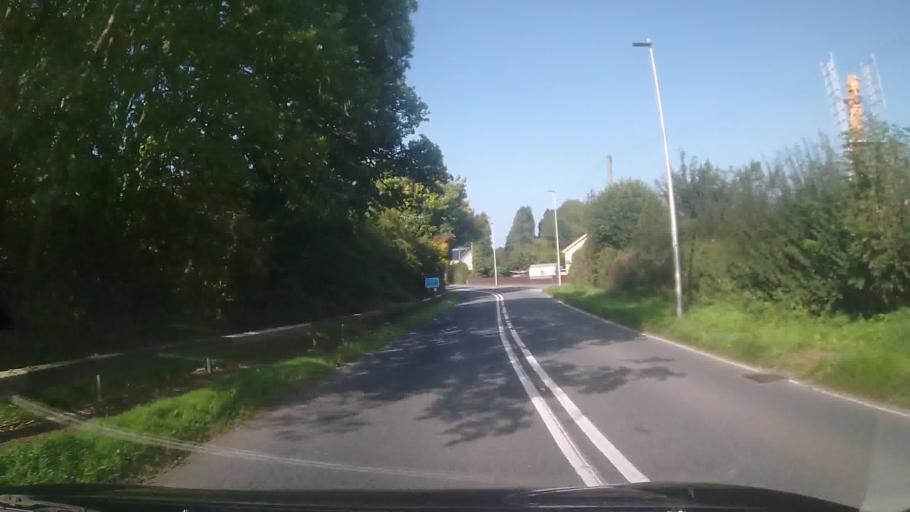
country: GB
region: Wales
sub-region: Sir Powys
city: Builth Wells
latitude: 52.1517
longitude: -3.4510
